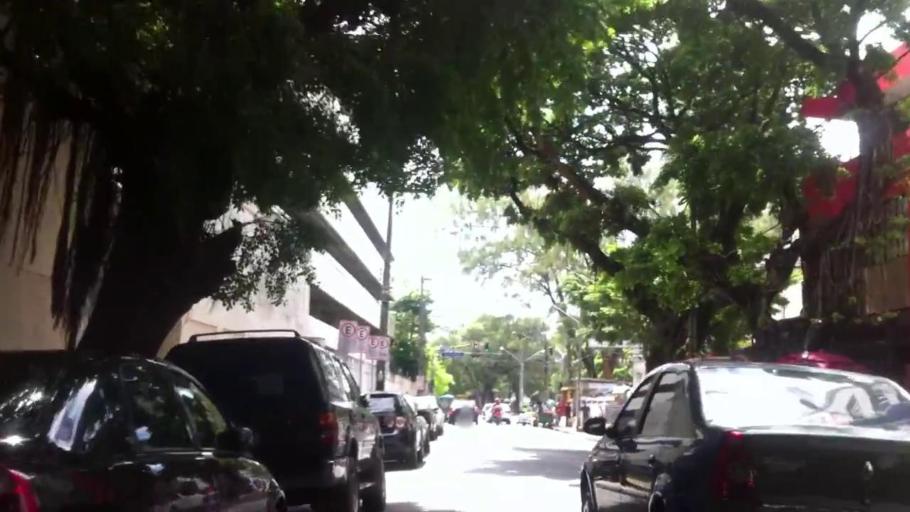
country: BR
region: Pernambuco
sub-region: Recife
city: Recife
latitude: -8.0593
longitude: -34.8833
